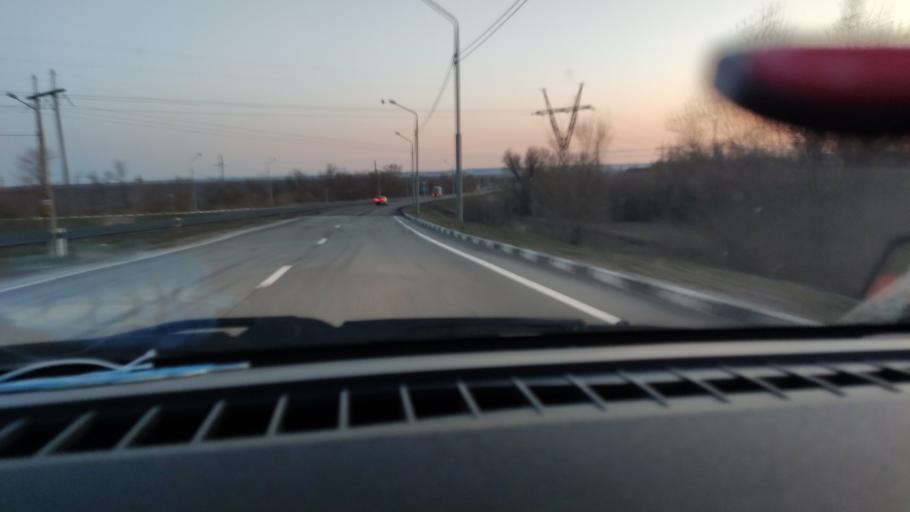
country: RU
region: Saratov
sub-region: Saratovskiy Rayon
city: Saratov
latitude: 51.6713
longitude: 46.0010
